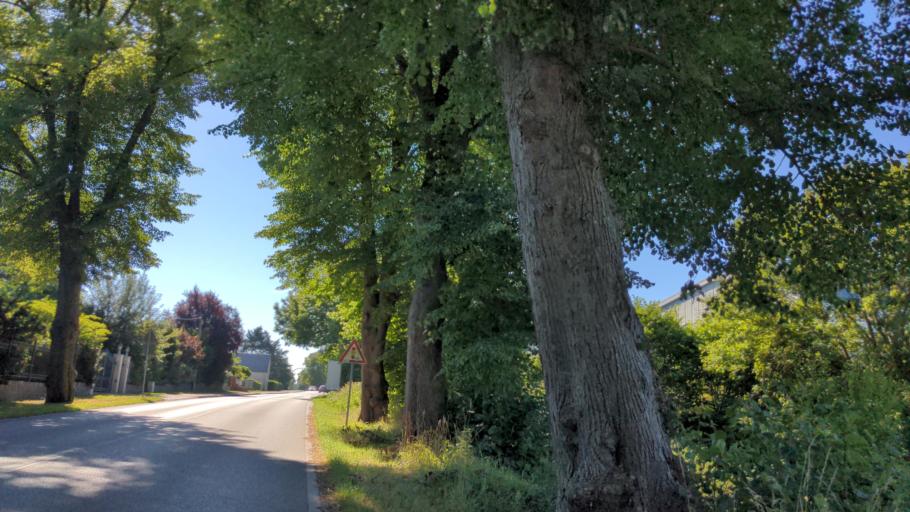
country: DE
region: Mecklenburg-Vorpommern
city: Selmsdorf
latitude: 53.8538
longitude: 10.9218
